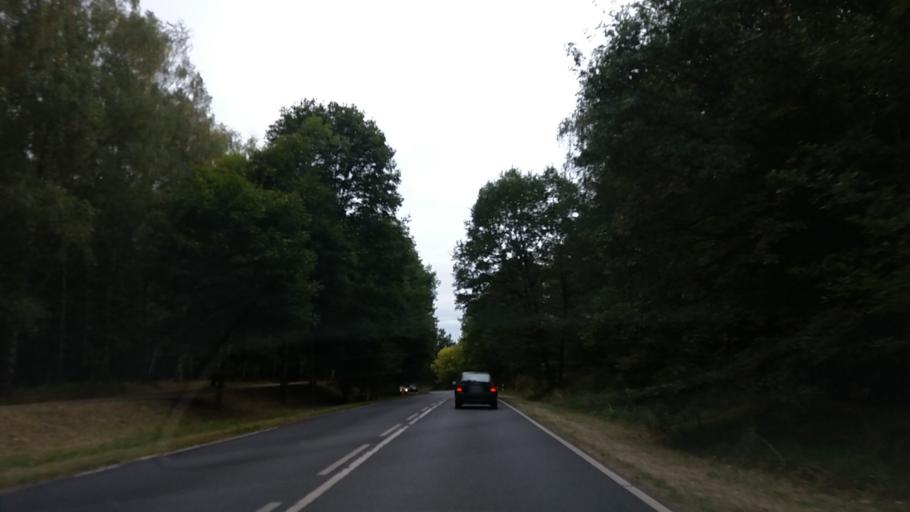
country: PL
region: Lubusz
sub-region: Powiat gorzowski
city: Klodawa
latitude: 52.7679
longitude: 15.2289
